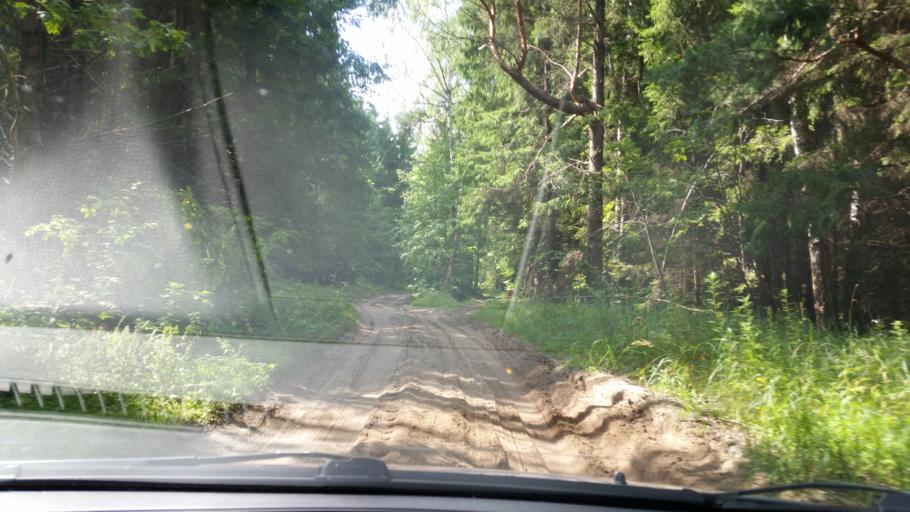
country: RU
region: Moskovskaya
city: Pushchino
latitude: 54.9263
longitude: 37.7017
